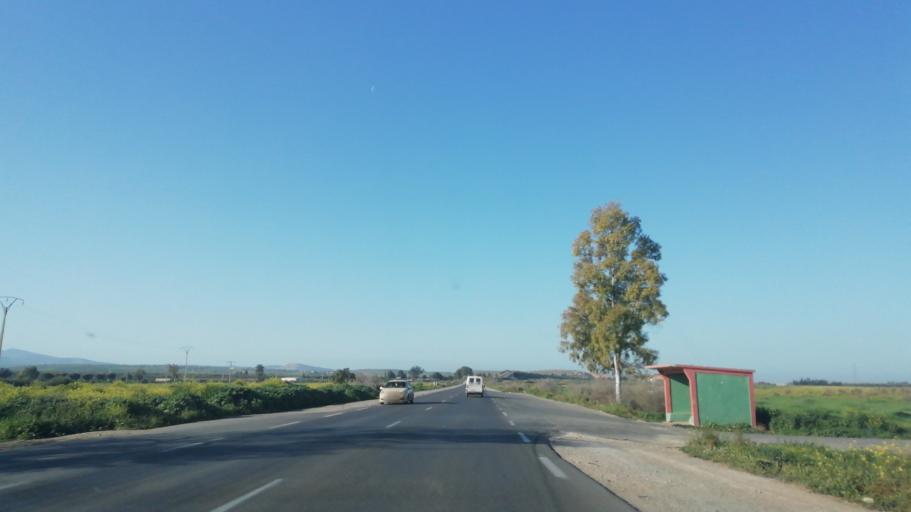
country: DZ
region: Mascara
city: Mascara
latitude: 35.6560
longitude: 0.1918
